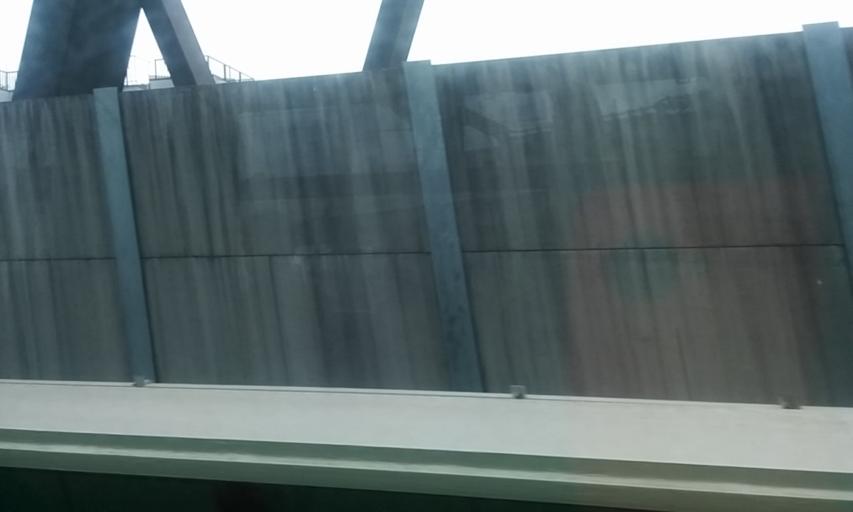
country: JP
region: Osaka
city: Moriguchi
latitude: 34.6876
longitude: 135.5708
